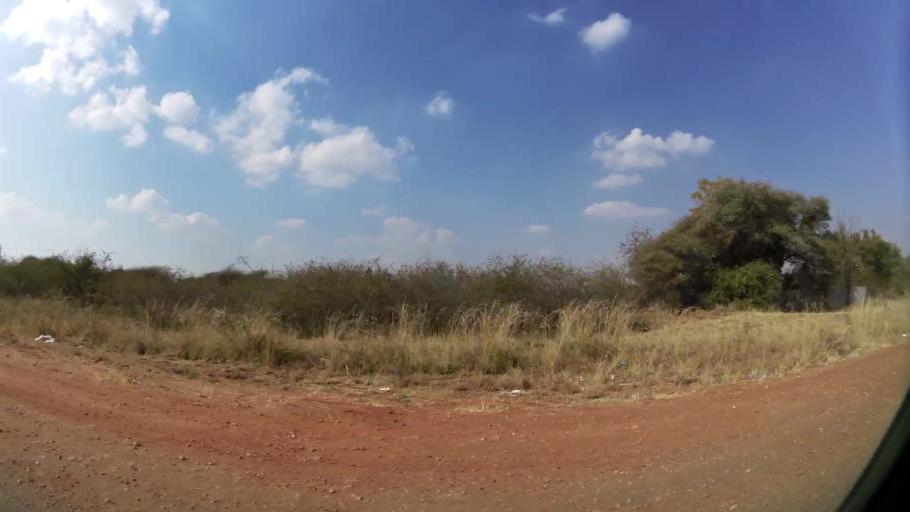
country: ZA
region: North-West
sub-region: Bojanala Platinum District Municipality
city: Rustenburg
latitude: -25.4821
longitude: 27.0864
